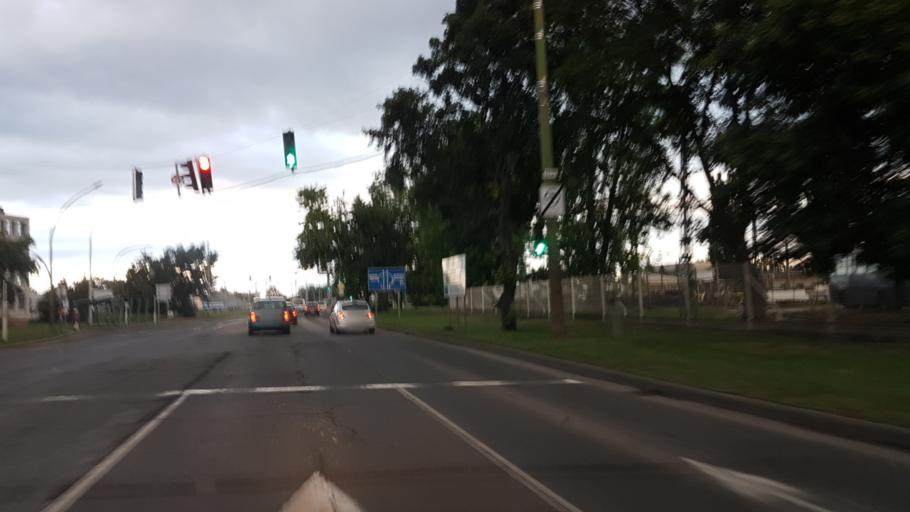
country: HU
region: Borsod-Abauj-Zemplen
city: Miskolc
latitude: 48.1068
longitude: 20.8168
